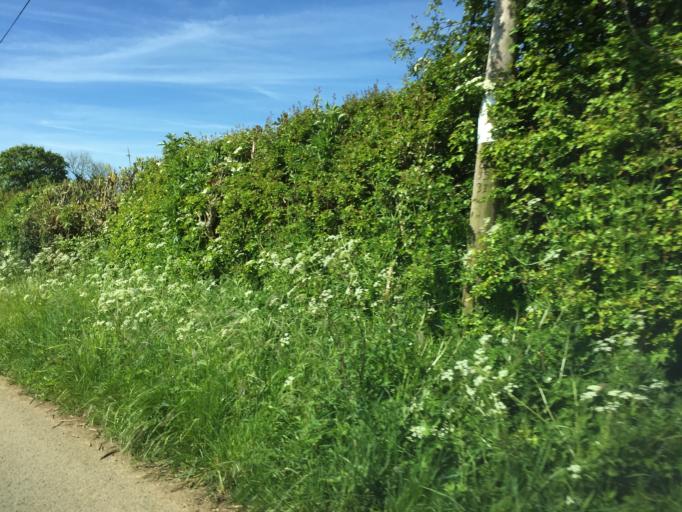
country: GB
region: England
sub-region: Wiltshire
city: Luckington
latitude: 51.6152
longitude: -2.2576
